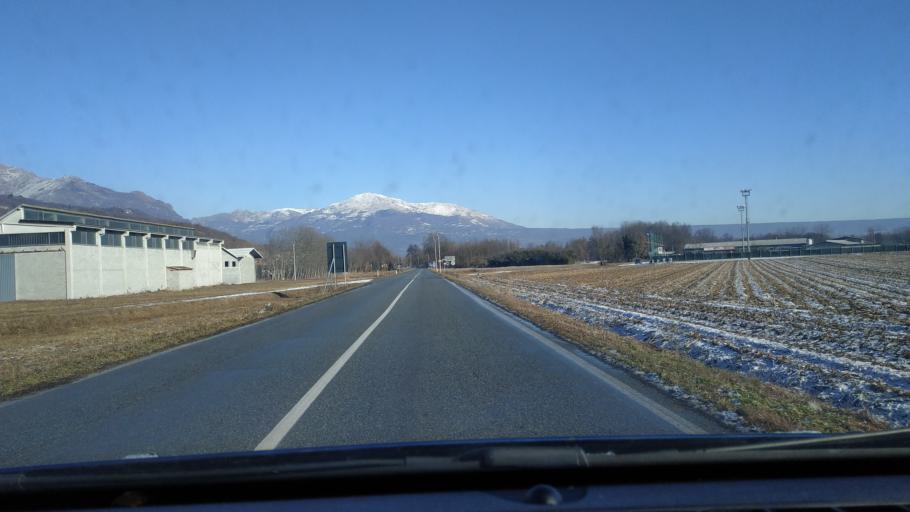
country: IT
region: Piedmont
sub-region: Provincia di Torino
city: Colleretto Giacosa
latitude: 45.4282
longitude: 7.8011
